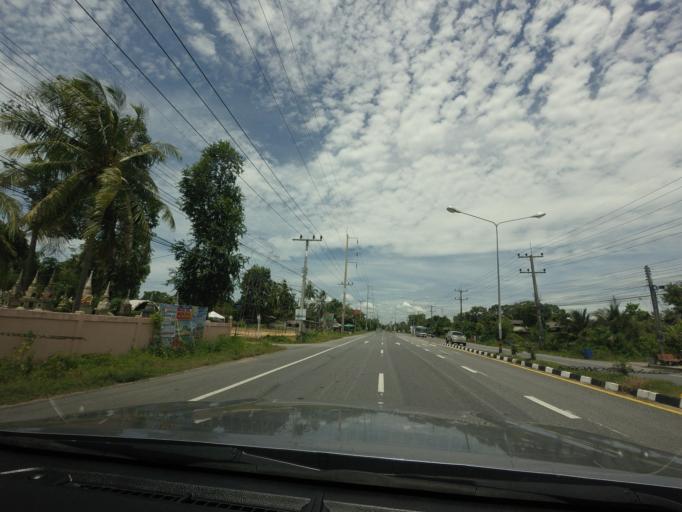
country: TH
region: Songkhla
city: Sathing Phra
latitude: 7.5637
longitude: 100.4120
